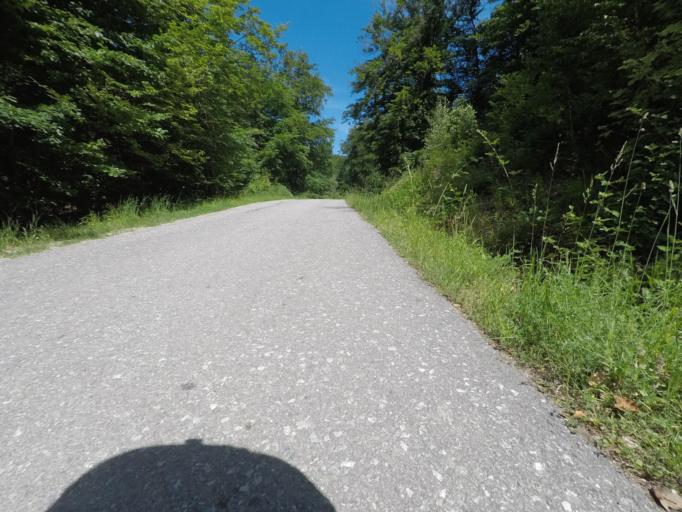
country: AT
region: Lower Austria
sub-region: Politischer Bezirk Modling
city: Perchtoldsdorf
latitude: 48.1750
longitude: 16.2395
